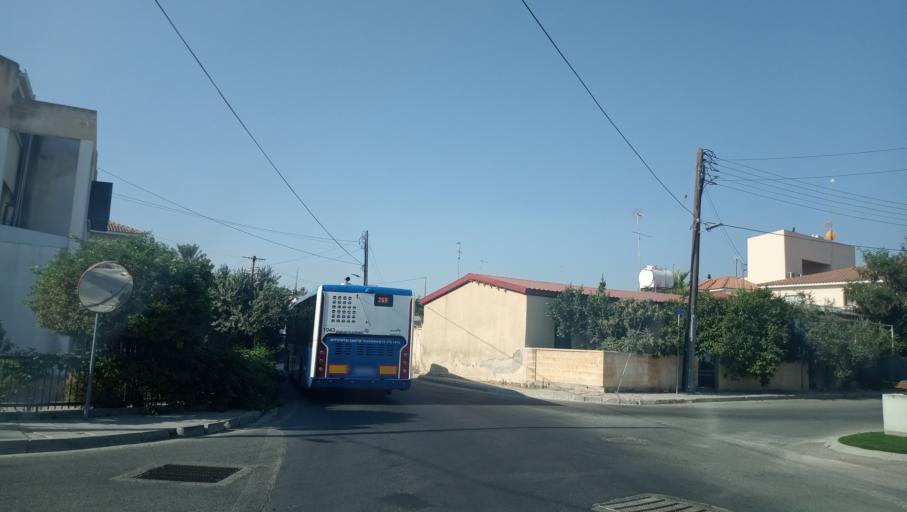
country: CY
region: Lefkosia
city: Geri
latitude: 35.1079
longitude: 33.4244
